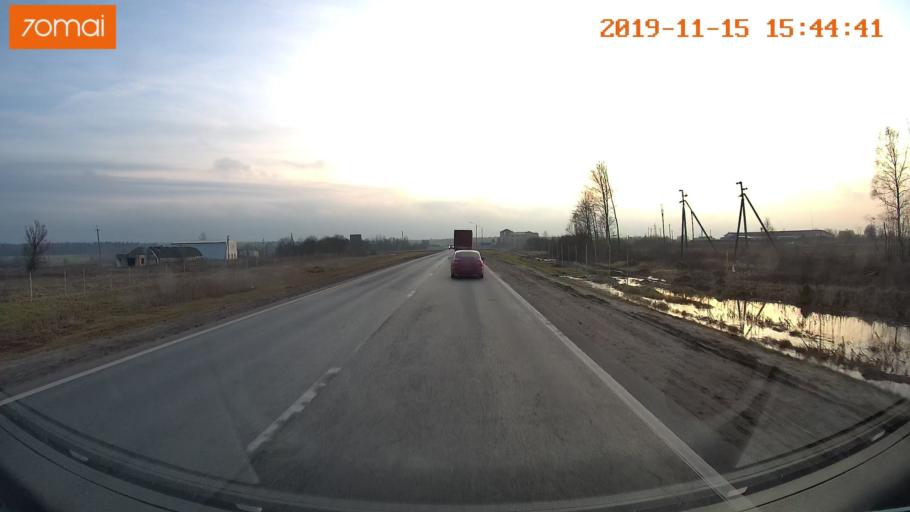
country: RU
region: Jaroslavl
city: Danilov
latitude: 57.9676
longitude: 40.0197
